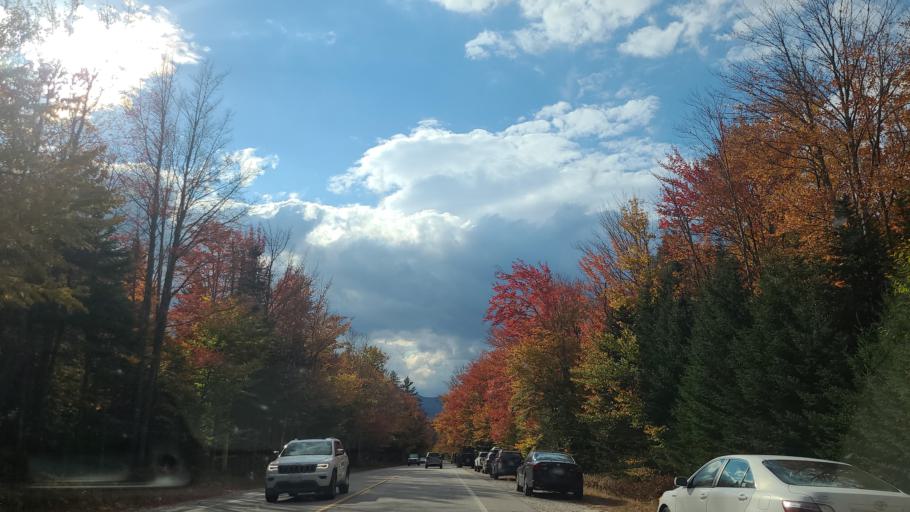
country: US
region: New Hampshire
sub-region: Carroll County
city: Tamworth
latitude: 43.9902
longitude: -71.3002
